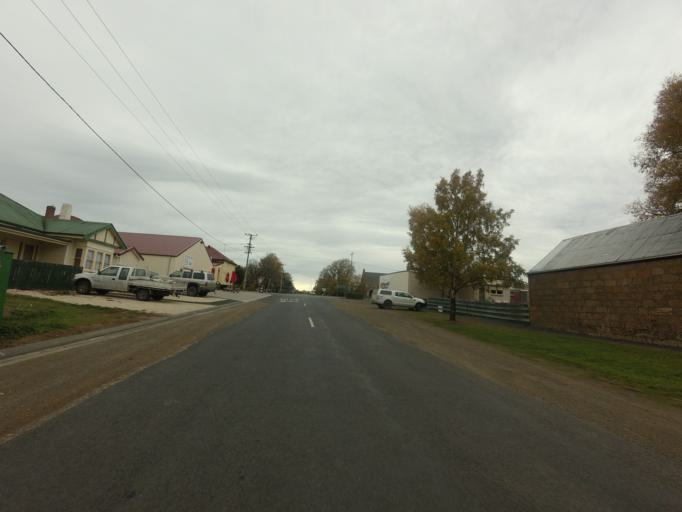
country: AU
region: Tasmania
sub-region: Derwent Valley
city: New Norfolk
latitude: -42.3848
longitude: 147.0075
